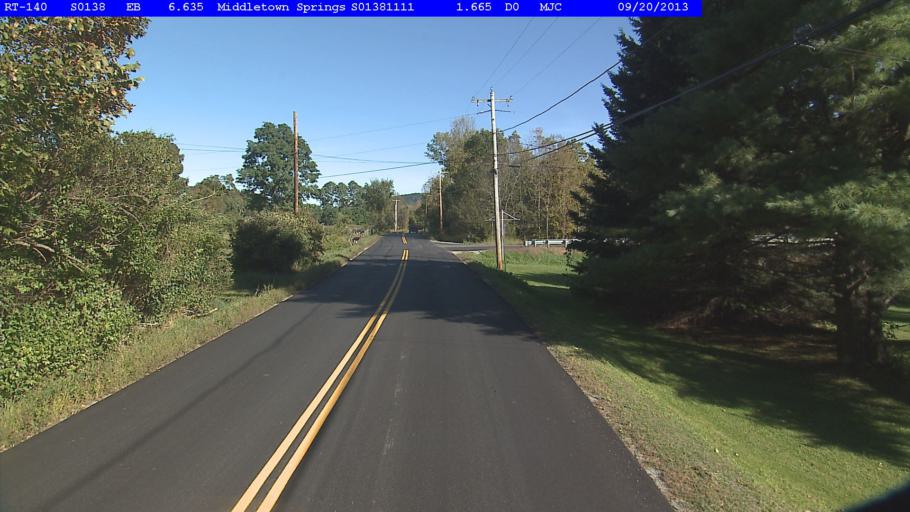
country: US
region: Vermont
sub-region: Rutland County
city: Poultney
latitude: 43.4844
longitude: -73.1483
